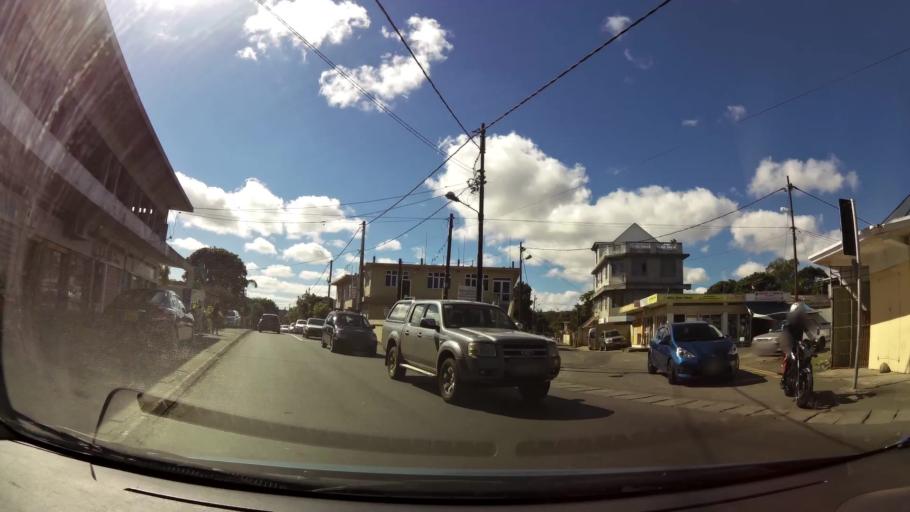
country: MU
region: Plaines Wilhems
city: Vacoas
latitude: -20.3130
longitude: 57.4878
